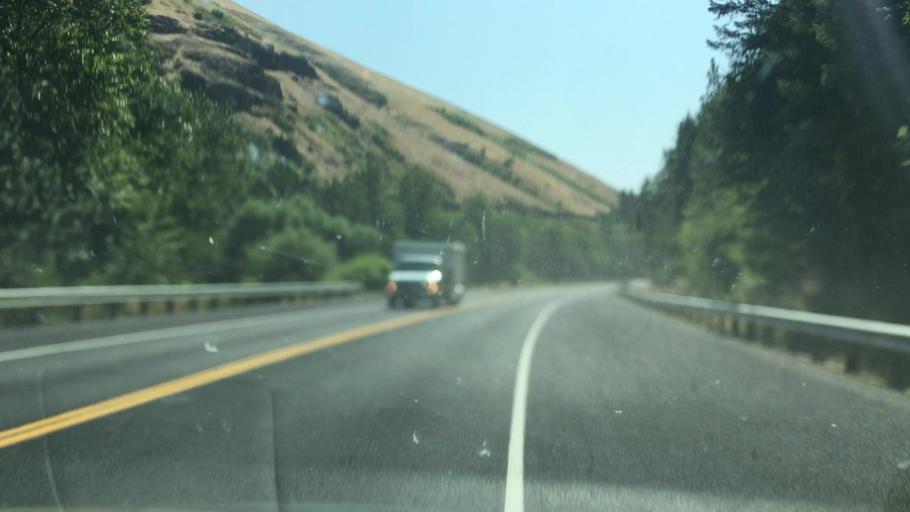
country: US
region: Idaho
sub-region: Nez Perce County
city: Lapwai
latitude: 46.3537
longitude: -116.6238
